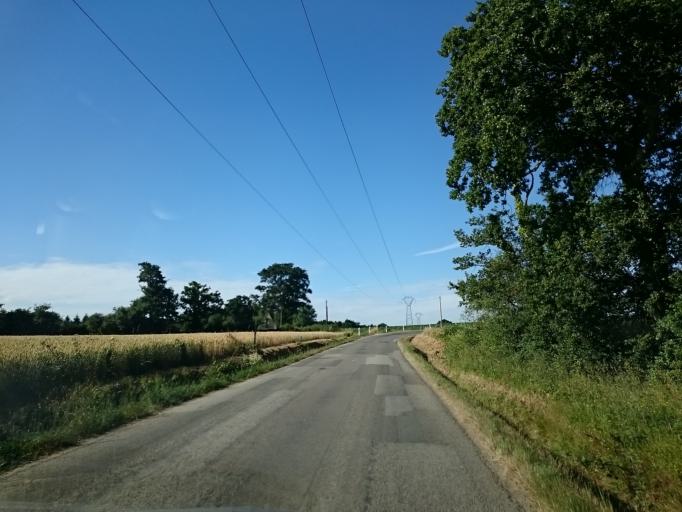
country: FR
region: Brittany
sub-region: Departement d'Ille-et-Vilaine
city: Chanteloup
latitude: 47.9691
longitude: -1.6025
